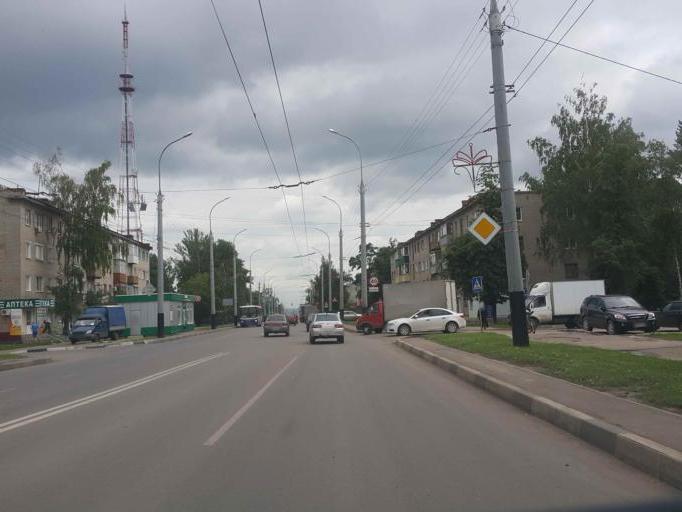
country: RU
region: Tambov
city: Tambov
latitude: 52.7467
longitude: 41.4212
